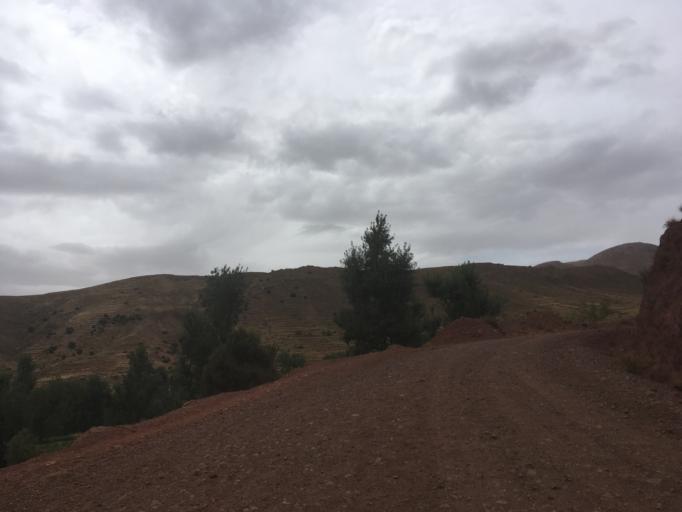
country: MA
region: Marrakech-Tensift-Al Haouz
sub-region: Al-Haouz
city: Tidili Mesfioua
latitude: 31.3854
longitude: -7.5796
